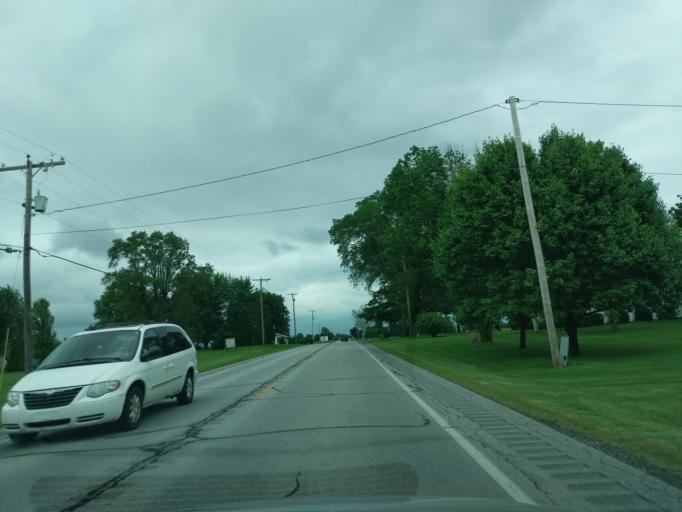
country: US
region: Indiana
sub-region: Madison County
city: Elwood
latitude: 40.2774
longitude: -85.8000
